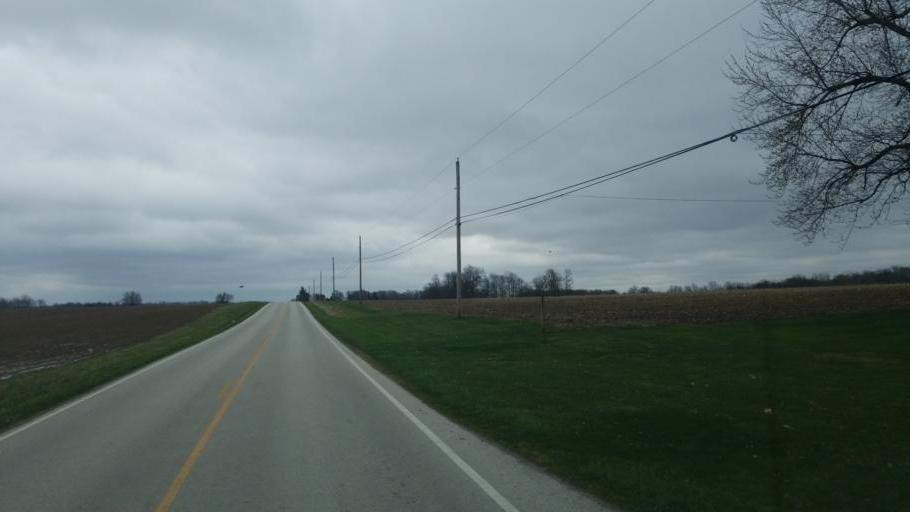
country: US
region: Ohio
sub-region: Wyandot County
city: Upper Sandusky
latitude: 40.8258
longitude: -83.2132
